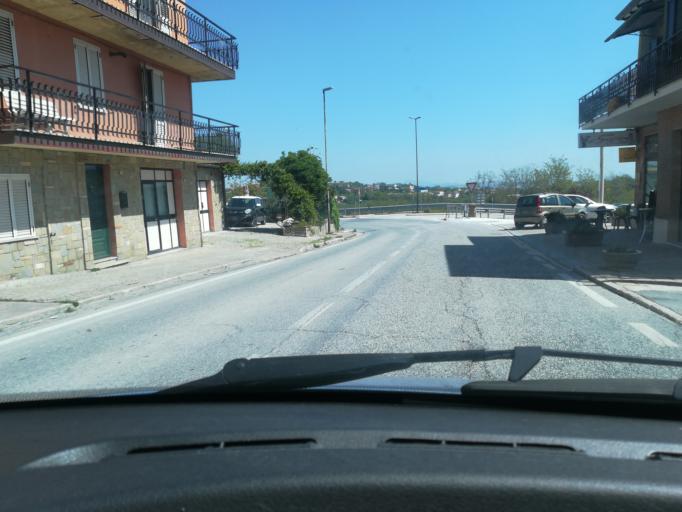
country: IT
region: The Marches
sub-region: Provincia di Macerata
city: Strada
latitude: 43.3983
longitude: 13.2102
